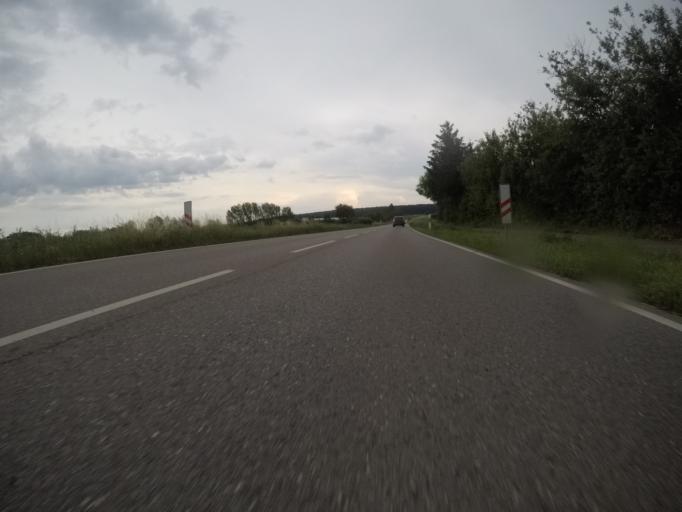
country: DE
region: Baden-Wuerttemberg
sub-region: Regierungsbezirk Stuttgart
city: Eberdingen
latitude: 48.8463
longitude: 8.9794
